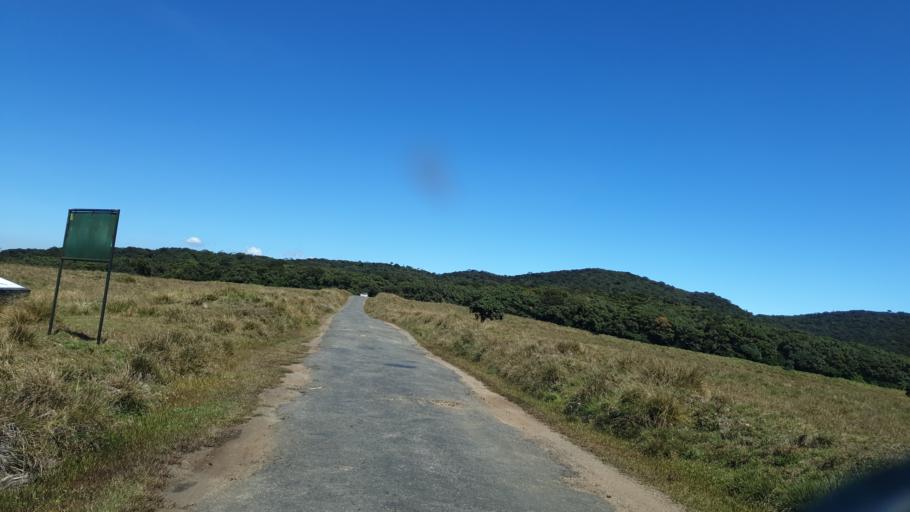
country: LK
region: Central
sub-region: Nuwara Eliya District
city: Nuwara Eliya
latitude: 6.8233
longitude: 80.8056
